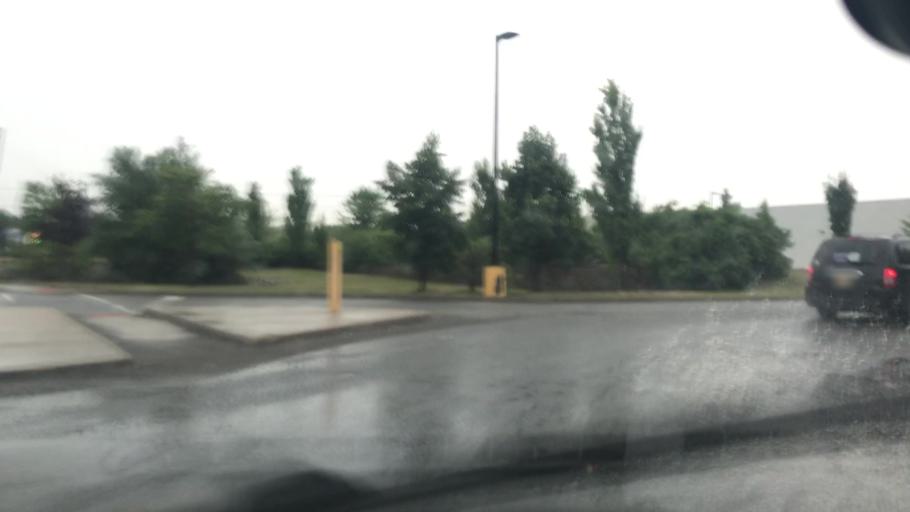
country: US
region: New Jersey
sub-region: Hudson County
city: Harrison
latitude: 40.7490
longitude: -74.1388
